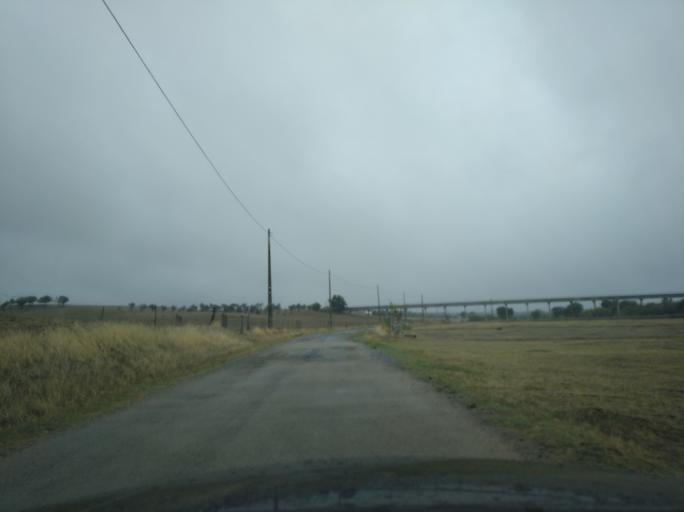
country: PT
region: Portalegre
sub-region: Campo Maior
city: Campo Maior
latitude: 38.9752
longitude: -7.0693
